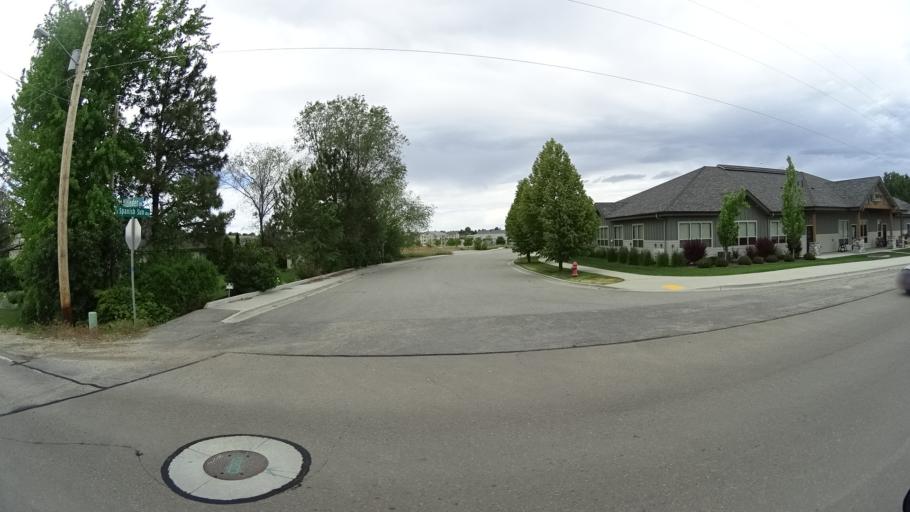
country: US
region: Idaho
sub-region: Ada County
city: Meridian
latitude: 43.5883
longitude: -116.4137
